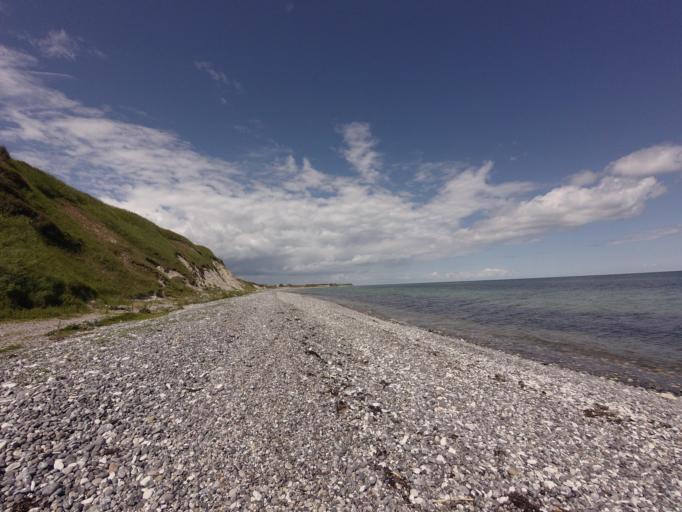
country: DK
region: Central Jutland
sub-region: Norddjurs Kommune
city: Grenaa
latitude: 56.5177
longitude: 10.8613
